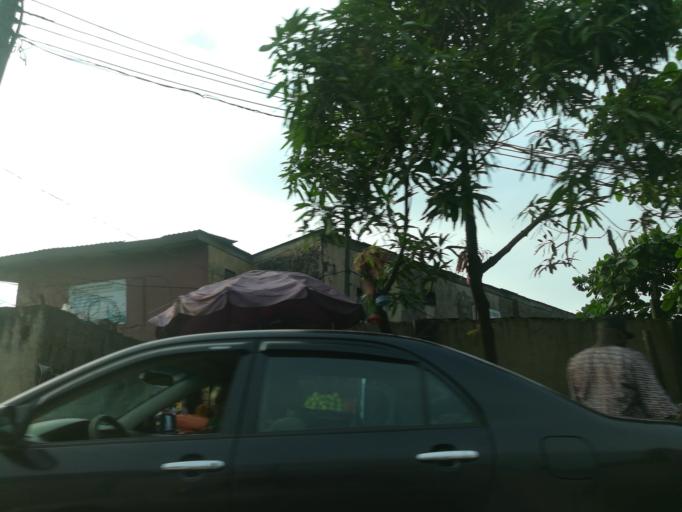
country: NG
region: Lagos
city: Ojota
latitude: 6.5962
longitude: 3.3845
